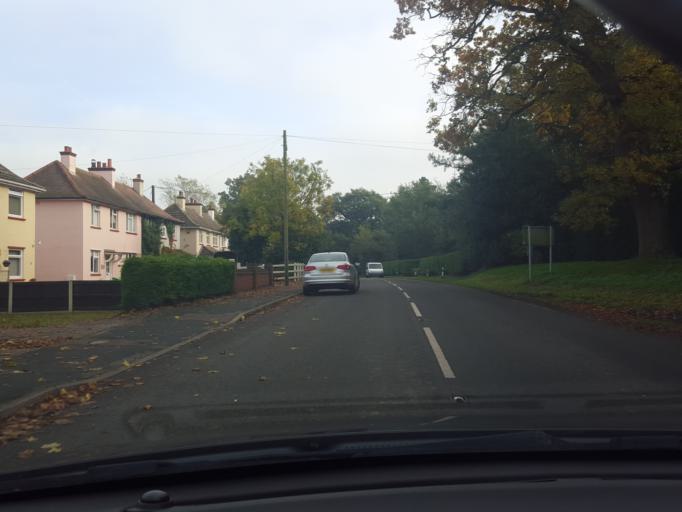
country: GB
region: England
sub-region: Essex
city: Mistley
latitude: 51.9344
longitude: 1.1184
